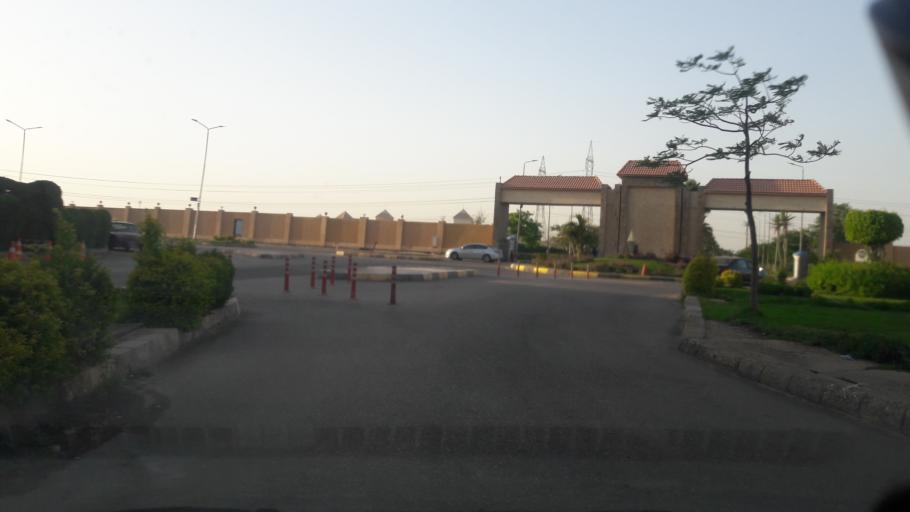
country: EG
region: Al Jizah
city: Madinat Sittah Uktubar
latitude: 29.9571
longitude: 31.0457
